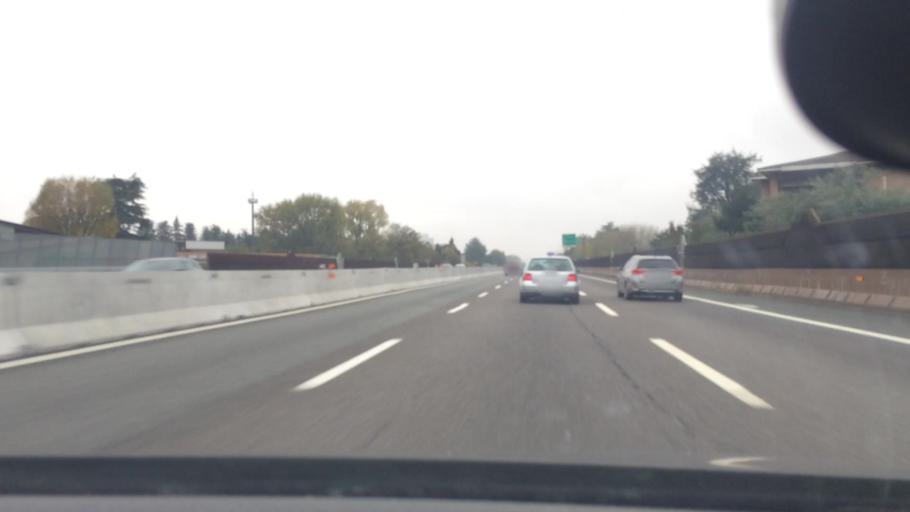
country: IT
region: Lombardy
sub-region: Citta metropolitana di Milano
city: Cerro Maggiore
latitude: 45.5976
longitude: 8.9583
